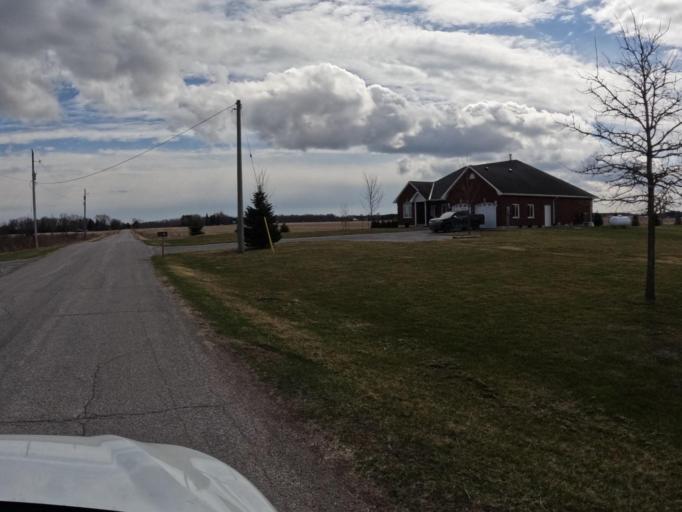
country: CA
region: Ontario
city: Norfolk County
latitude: 42.8703
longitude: -80.1938
